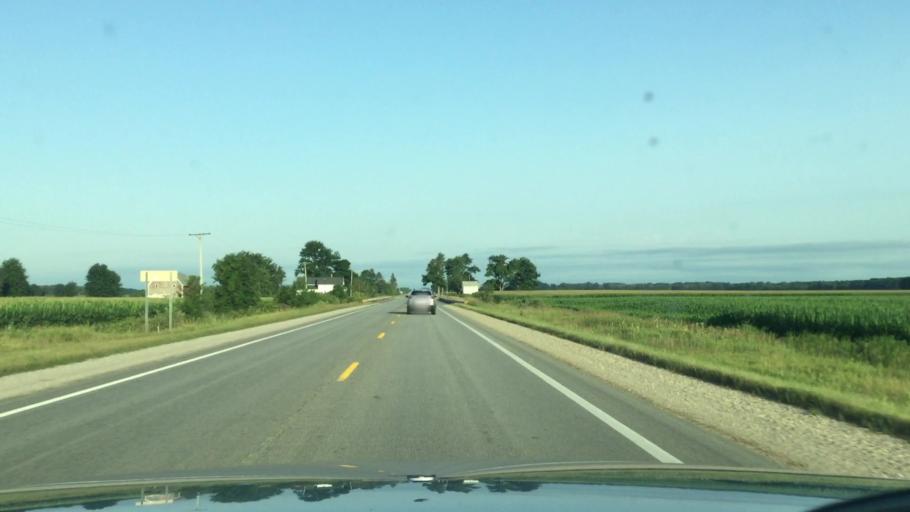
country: US
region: Michigan
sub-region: Montcalm County
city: Carson City
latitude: 43.1764
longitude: -84.7608
